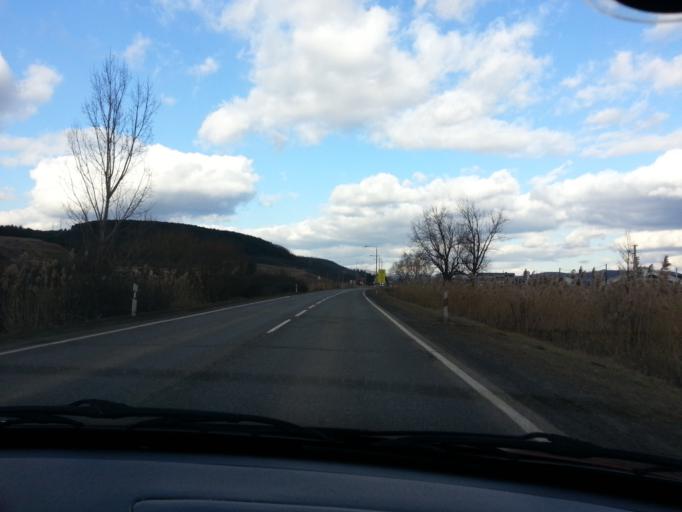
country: HU
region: Nograd
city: Batonyterenye
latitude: 47.9908
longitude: 19.8157
